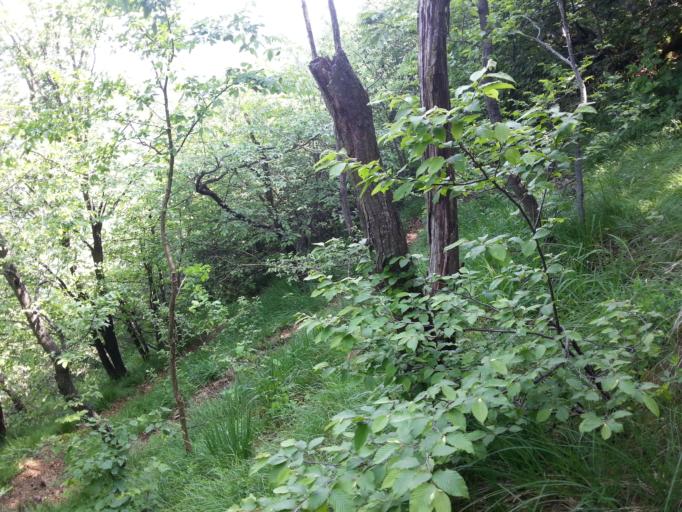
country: IT
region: Lombardy
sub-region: Provincia di Varese
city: Saltrio
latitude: 45.8925
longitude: 8.9240
